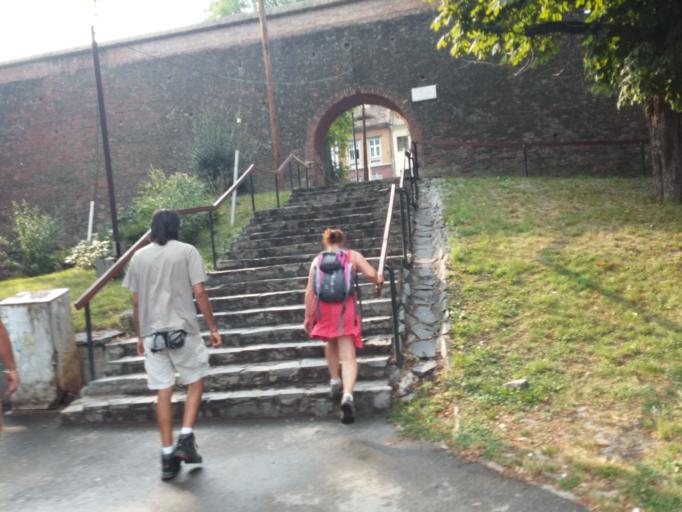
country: RO
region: Sibiu
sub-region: Municipiul Sibiu
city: Sibiu
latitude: 45.7923
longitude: 24.1506
